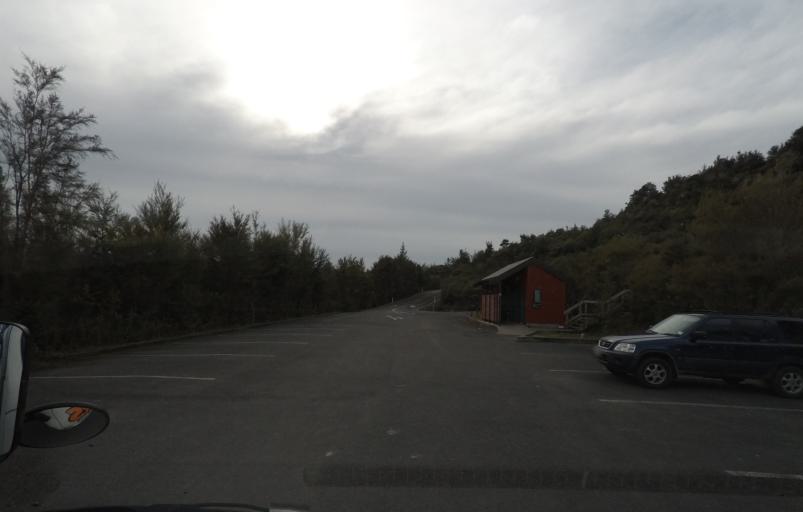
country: NZ
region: Tasman
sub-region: Tasman District
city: Takaka
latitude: -40.8480
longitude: 172.7706
